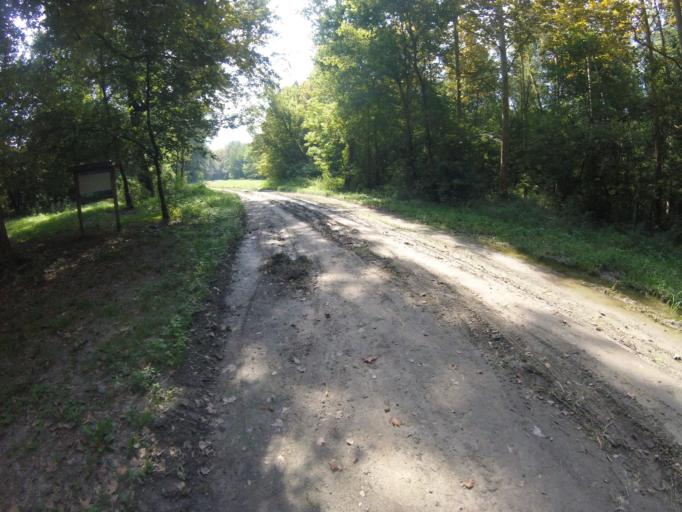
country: HU
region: Bacs-Kiskun
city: Baja
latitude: 46.2013
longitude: 18.8965
